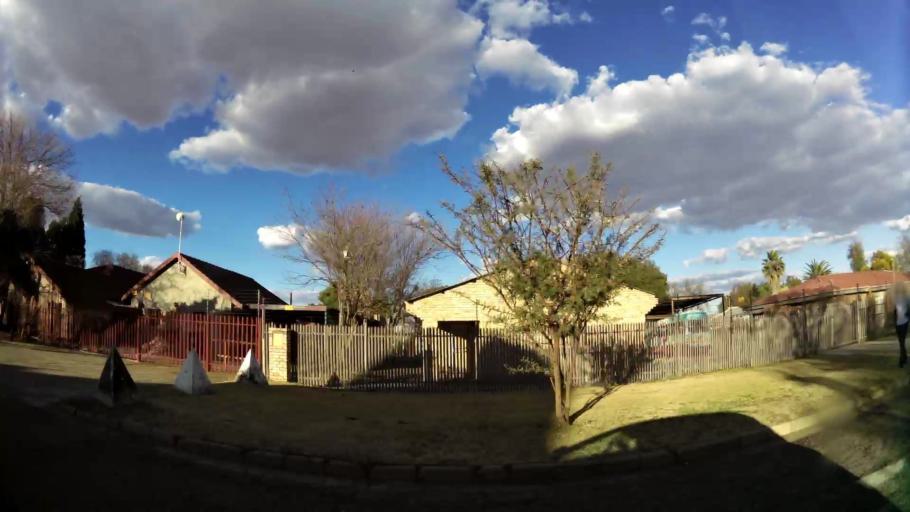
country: ZA
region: North-West
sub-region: Dr Kenneth Kaunda District Municipality
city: Potchefstroom
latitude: -26.7026
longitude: 27.0868
